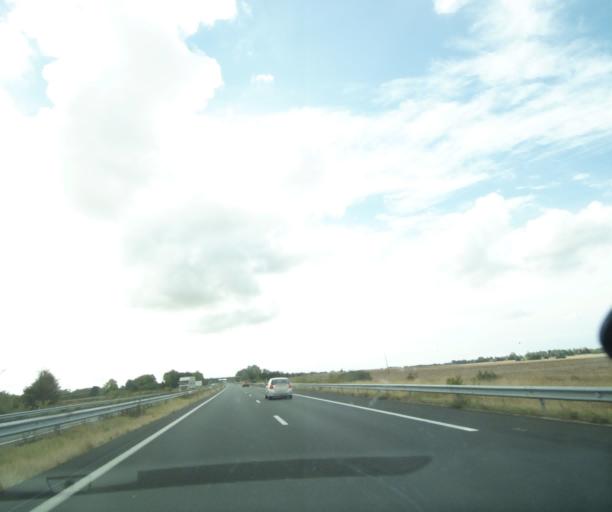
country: FR
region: Poitou-Charentes
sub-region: Departement de la Charente-Maritime
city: Thenac
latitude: 45.6831
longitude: -0.6447
